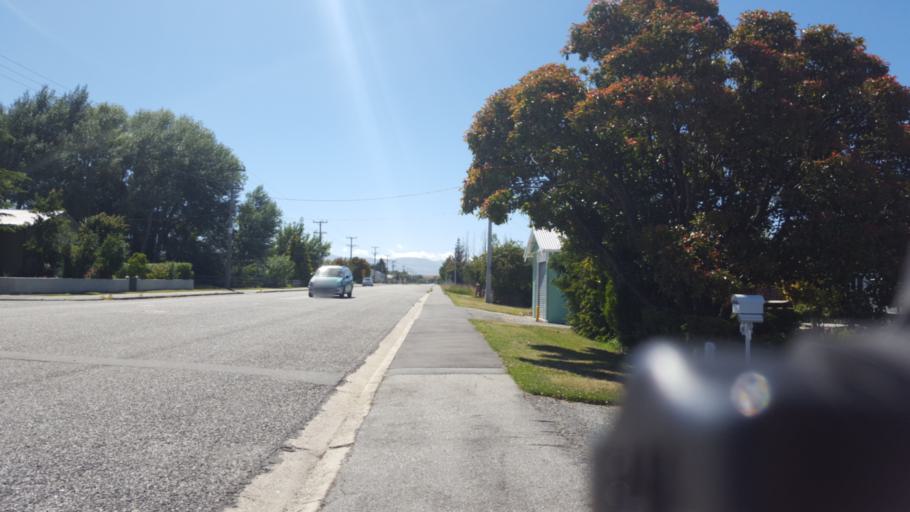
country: NZ
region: Otago
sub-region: Dunedin City
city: Dunedin
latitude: -45.1257
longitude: 170.0966
